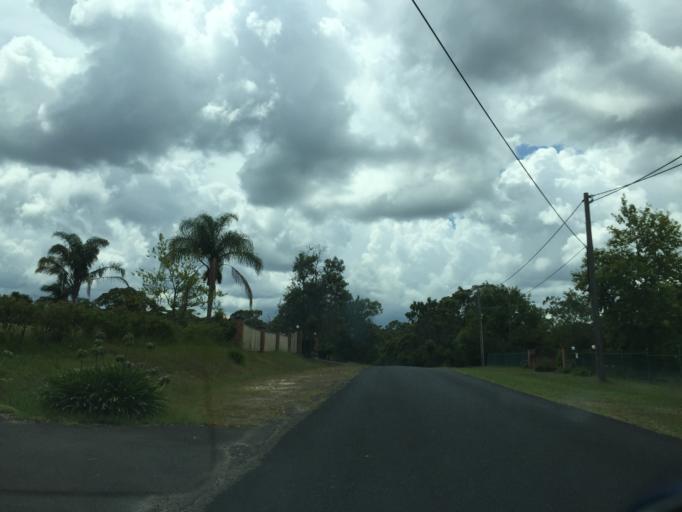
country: AU
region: New South Wales
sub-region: Hornsby Shire
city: Galston
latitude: -33.6589
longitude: 151.0478
